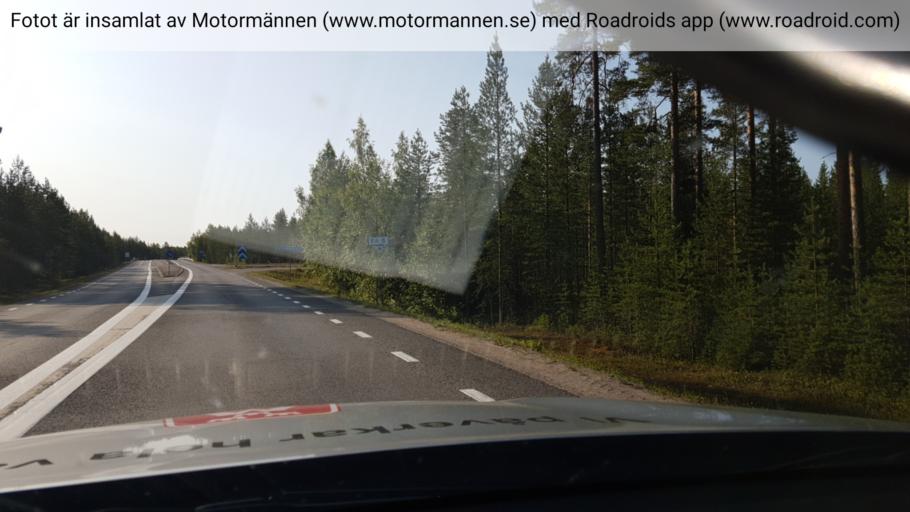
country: SE
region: Norrbotten
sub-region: Lulea Kommun
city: Gammelstad
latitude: 65.5999
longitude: 22.0394
